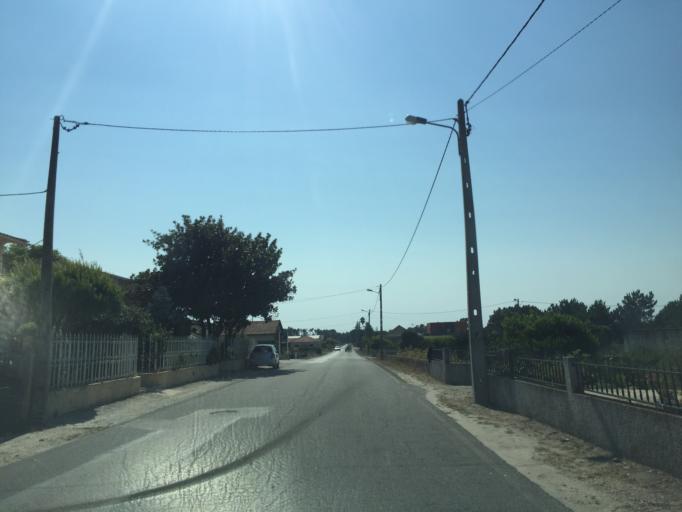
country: PT
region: Coimbra
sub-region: Montemor-O-Velho
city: Arazede
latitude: 40.3180
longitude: -8.7283
